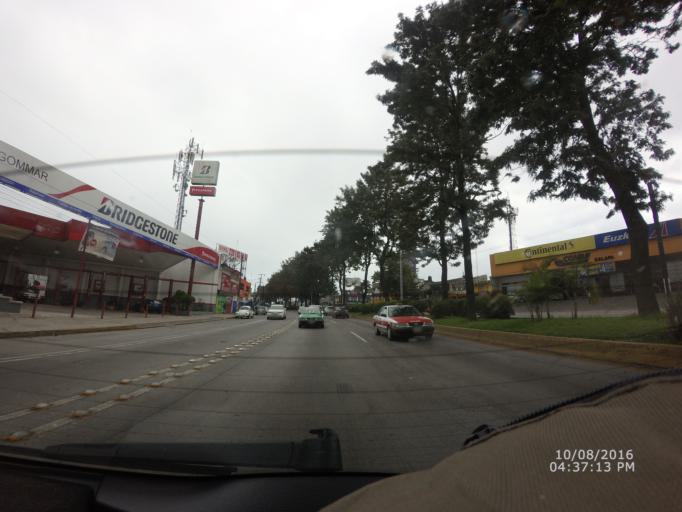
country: MX
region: Veracruz
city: Banderilla
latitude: 19.5619
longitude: -96.9269
